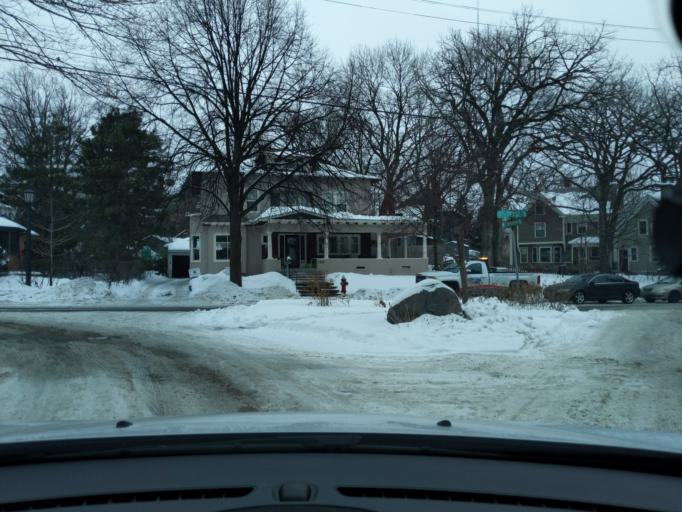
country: US
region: Minnesota
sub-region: Ramsey County
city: Lauderdale
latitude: 44.9661
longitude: -93.2099
